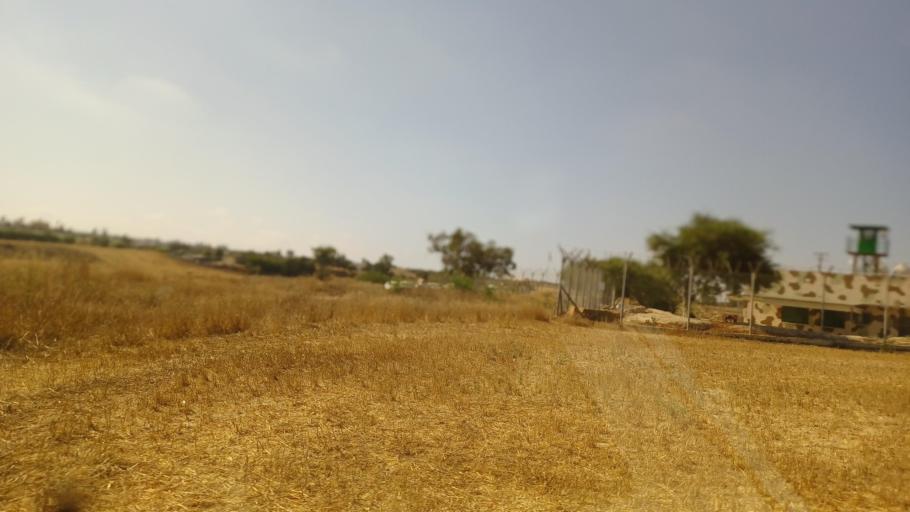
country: CY
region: Ammochostos
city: Acheritou
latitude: 35.0726
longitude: 33.8681
